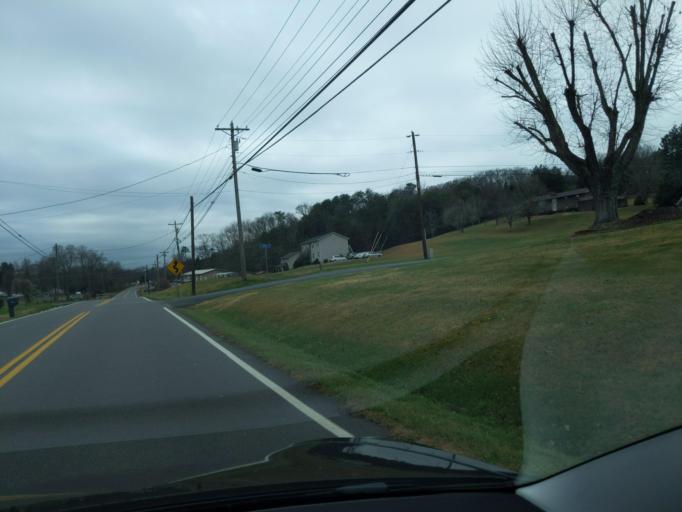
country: US
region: Tennessee
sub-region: Sevier County
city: Sevierville
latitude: 35.9620
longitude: -83.5798
